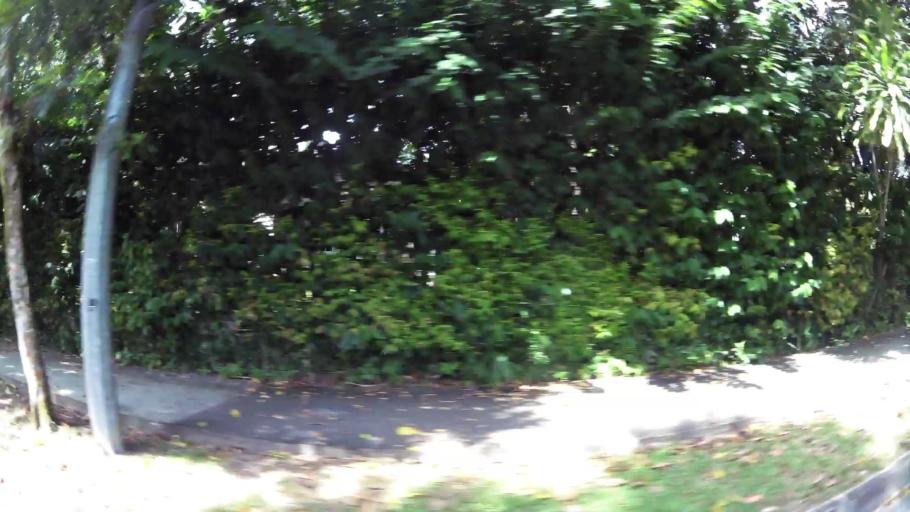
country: SG
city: Singapore
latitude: 1.3413
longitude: 103.7874
